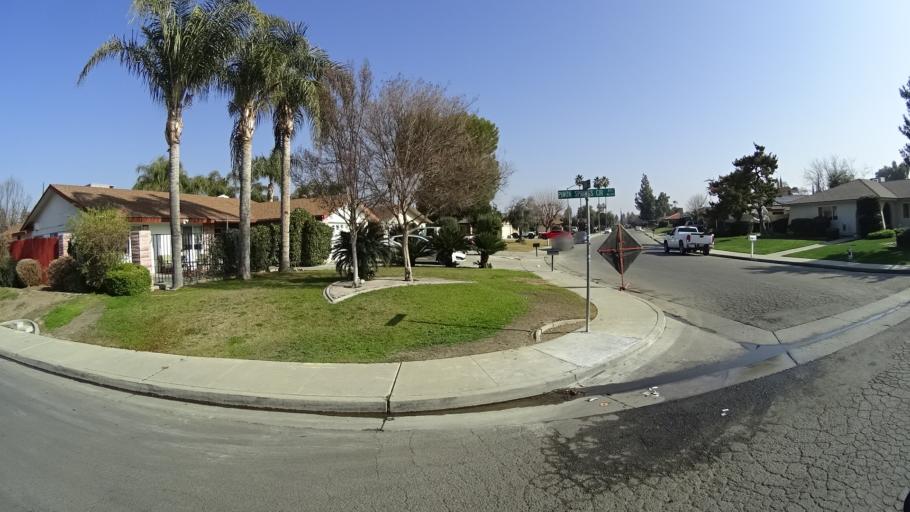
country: US
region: California
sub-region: Kern County
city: Greenacres
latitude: 35.3325
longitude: -119.0695
